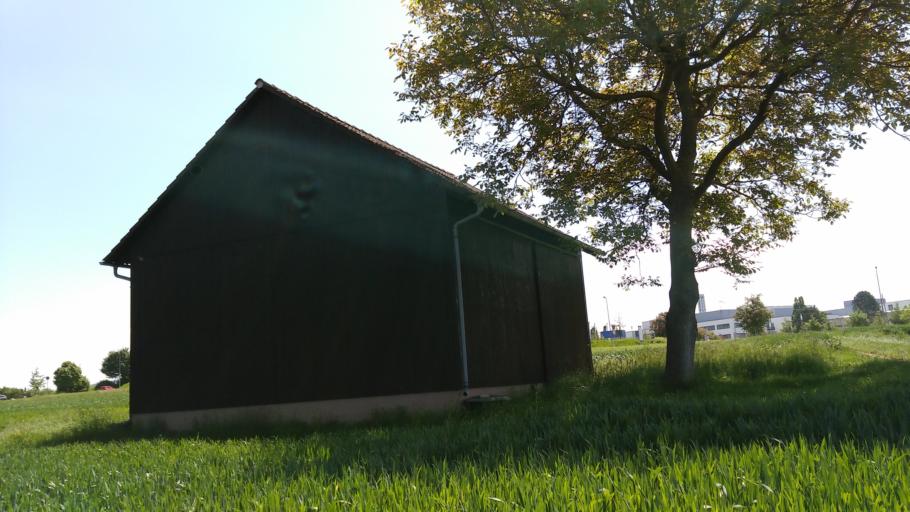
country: DE
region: Baden-Wuerttemberg
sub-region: Regierungsbezirk Stuttgart
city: Nurtingen
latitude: 48.6328
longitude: 9.3544
